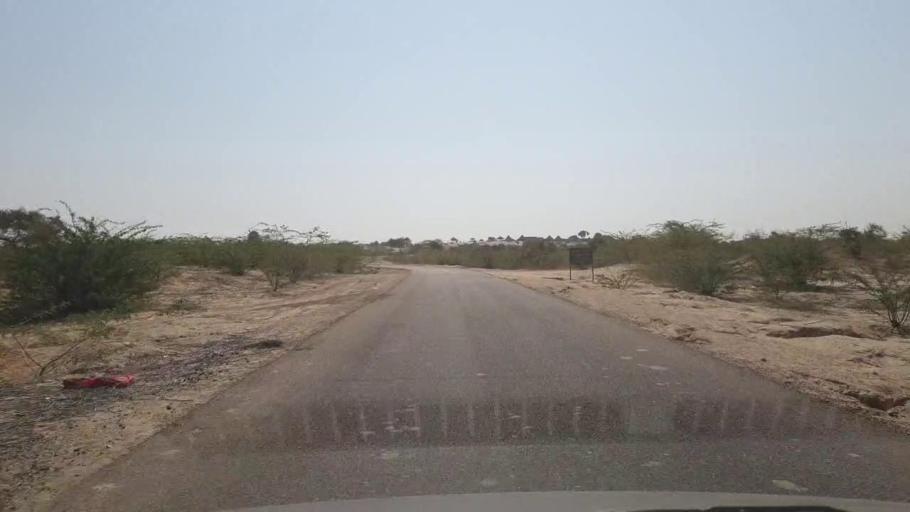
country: PK
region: Sindh
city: Chor
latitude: 25.5866
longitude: 70.1848
